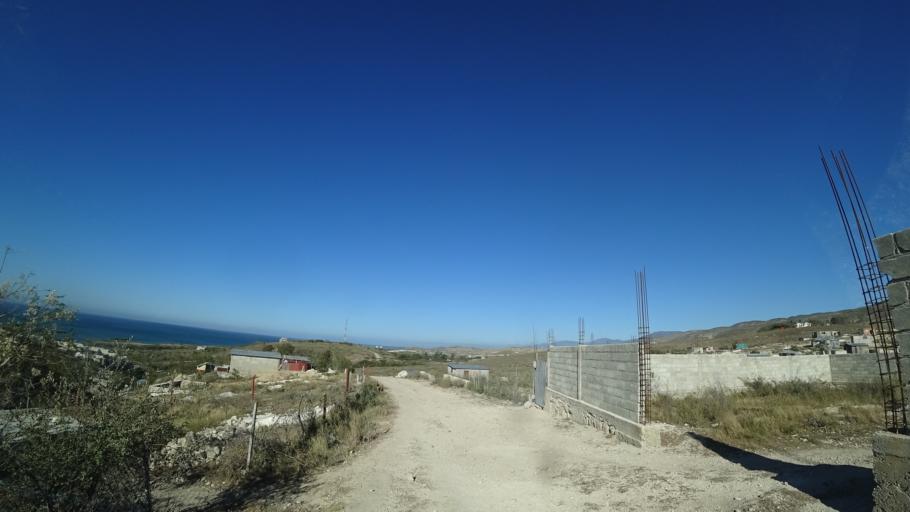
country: HT
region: Ouest
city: Cabaret
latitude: 18.6866
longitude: -72.3234
